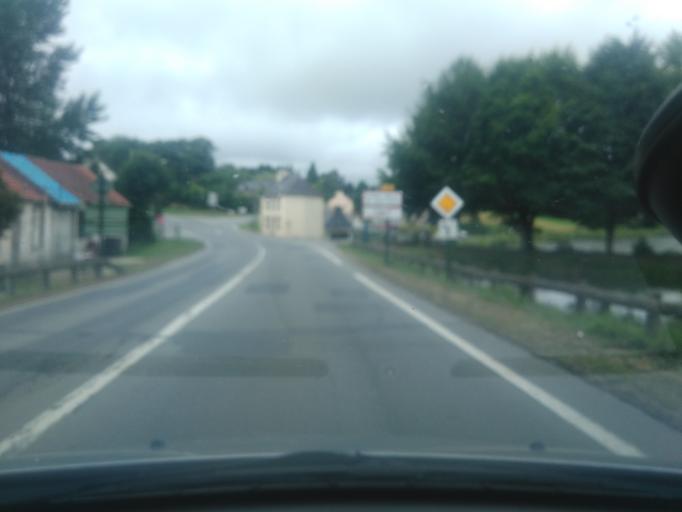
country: FR
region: Brittany
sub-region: Departement des Cotes-d'Armor
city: Corlay
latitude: 48.3179
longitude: -3.0614
